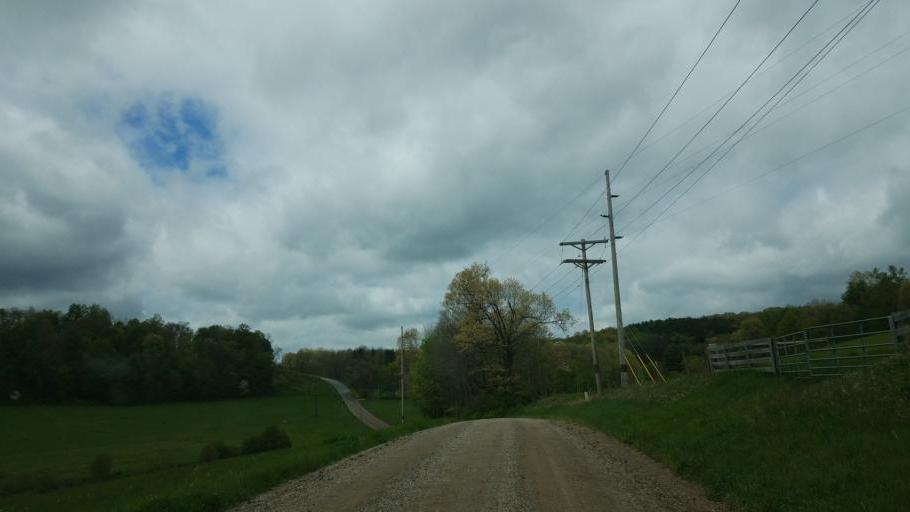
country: US
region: Ohio
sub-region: Ashland County
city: Loudonville
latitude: 40.5567
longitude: -82.3085
